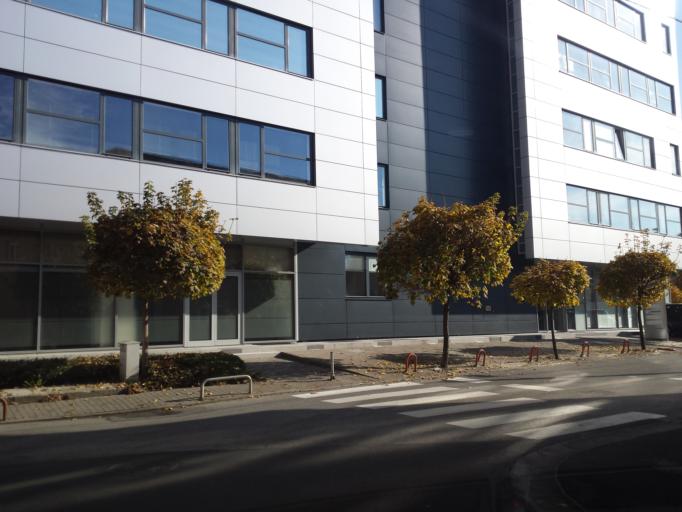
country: HR
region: Grad Zagreb
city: Zagreb - Centar
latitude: 45.8026
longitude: 15.9989
